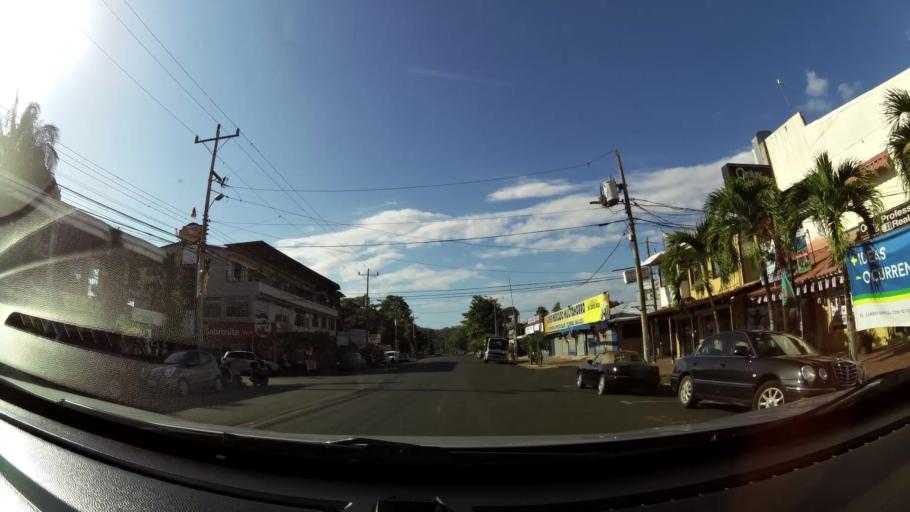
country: CR
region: Puntarenas
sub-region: Canton de Garabito
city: Jaco
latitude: 9.6184
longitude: -84.6325
